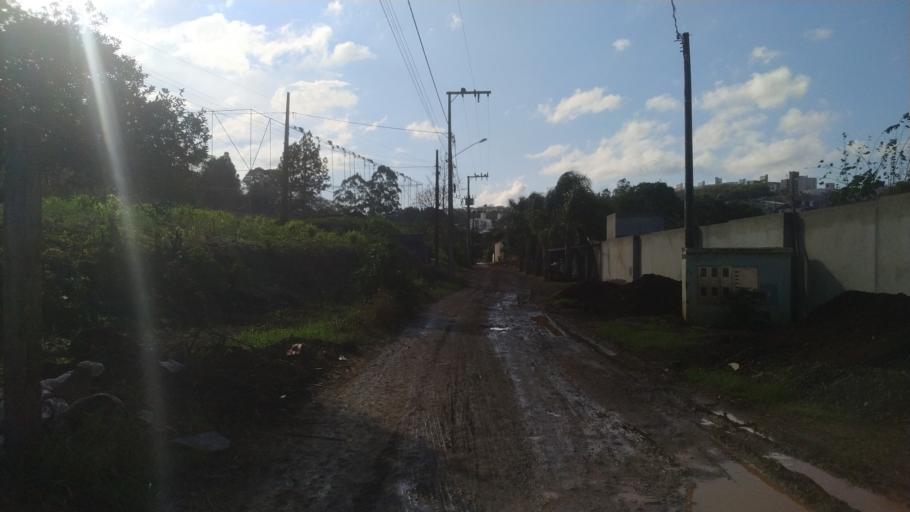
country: BR
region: Santa Catarina
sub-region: Chapeco
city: Chapeco
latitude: -27.0646
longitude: -52.6091
